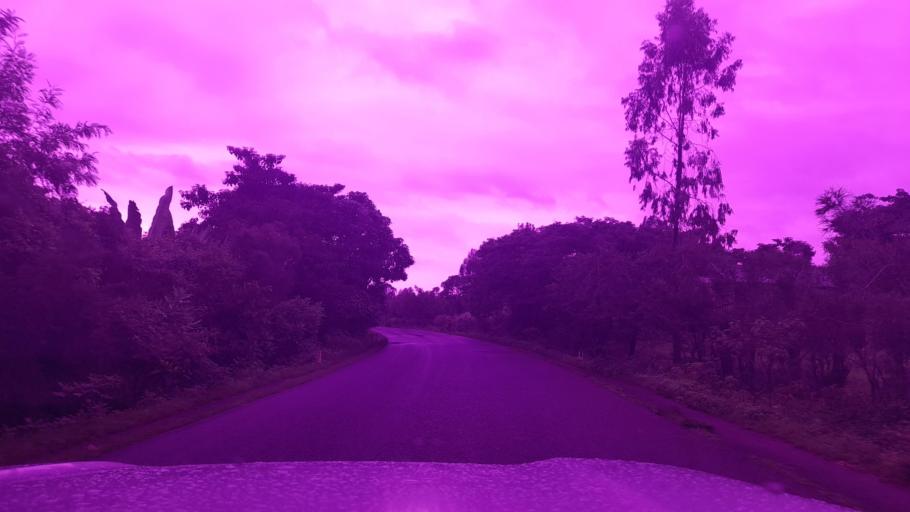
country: ET
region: Oromiya
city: Jima
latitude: 7.7121
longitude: 37.2521
